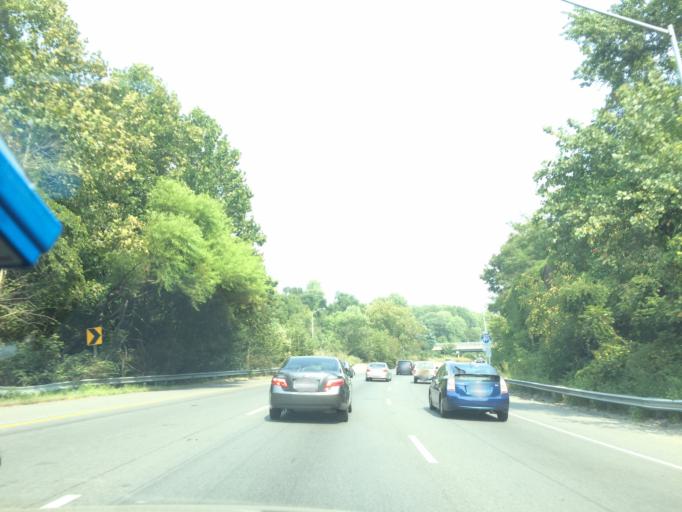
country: US
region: Maryland
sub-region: Montgomery County
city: Cabin John
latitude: 39.0128
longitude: -77.1483
